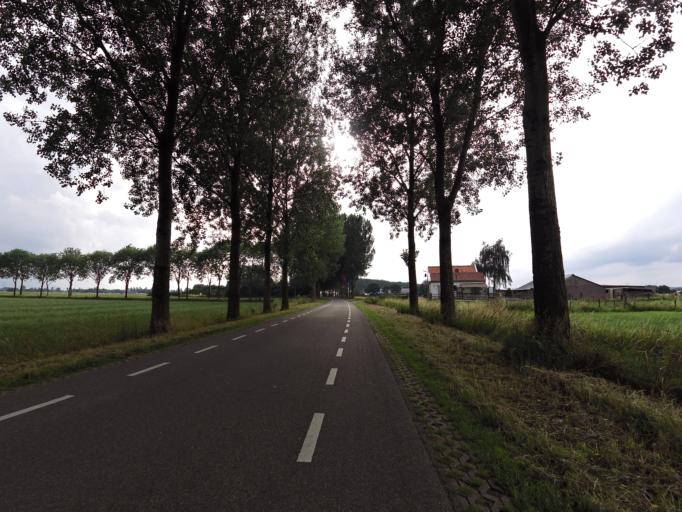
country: NL
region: Gelderland
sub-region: Gemeente Zevenaar
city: Zevenaar
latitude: 51.9699
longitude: 6.1004
